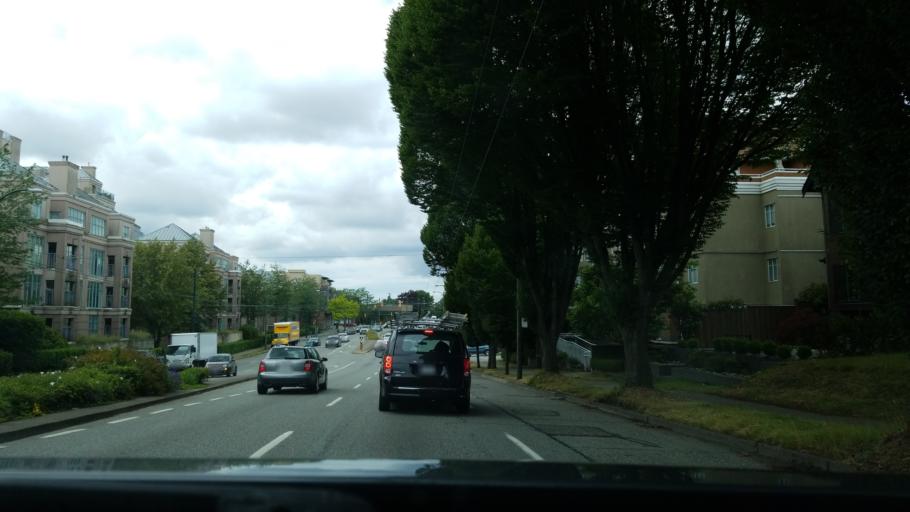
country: CA
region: British Columbia
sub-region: Fraser Valley Regional District
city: North Vancouver
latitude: 49.2621
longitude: -123.0536
